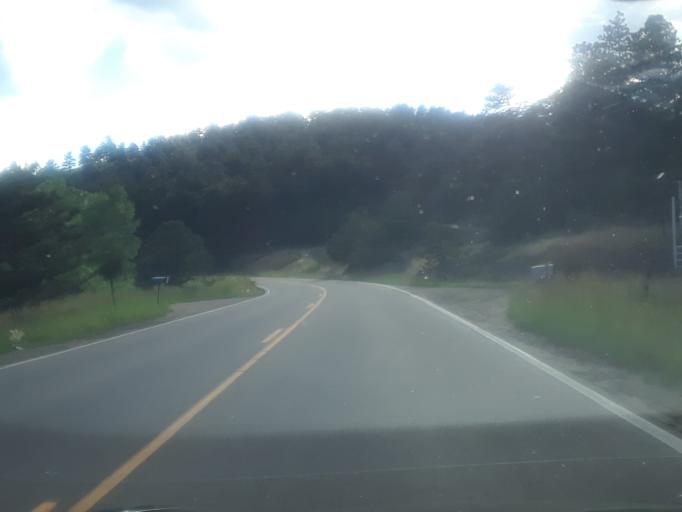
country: US
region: Colorado
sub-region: Jefferson County
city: Kittredge
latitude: 39.7186
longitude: -105.3728
